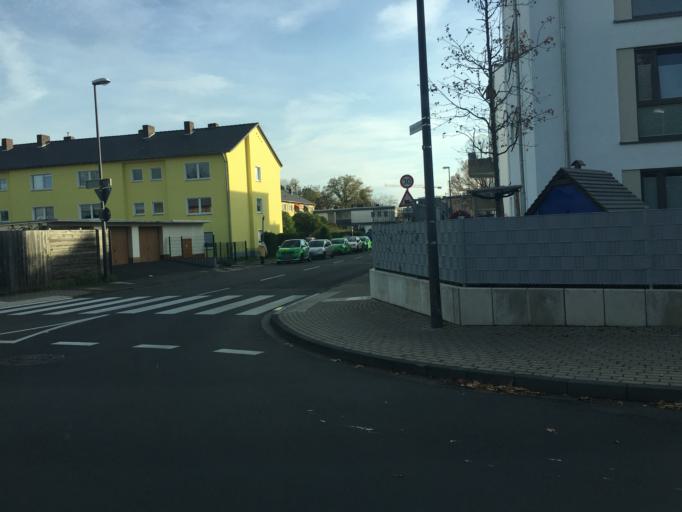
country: DE
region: North Rhine-Westphalia
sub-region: Regierungsbezirk Koln
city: Merheim
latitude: 50.9453
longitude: 7.0470
